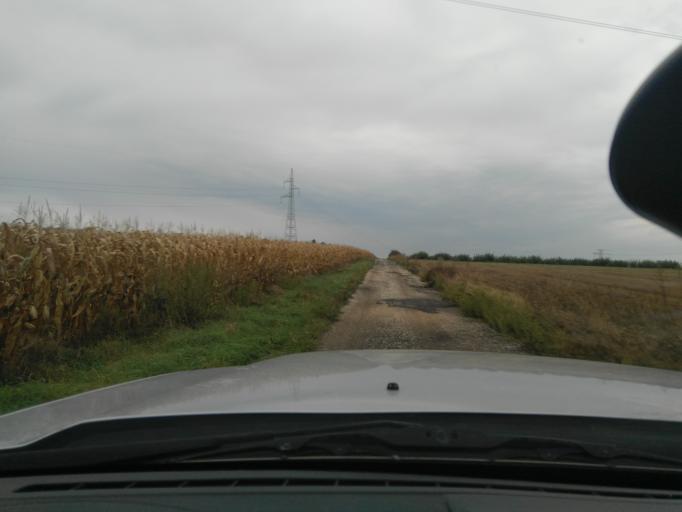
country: HU
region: Fejer
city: Martonvasar
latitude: 47.3508
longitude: 18.7639
